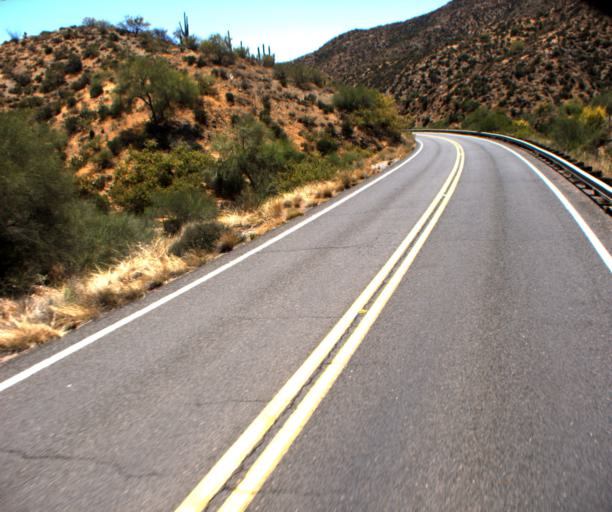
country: US
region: Arizona
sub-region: Pinal County
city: Superior
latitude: 33.1762
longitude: -111.0358
